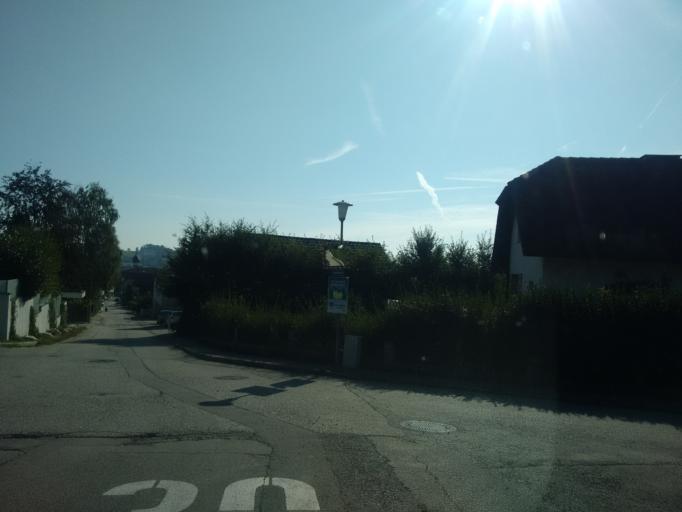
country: AT
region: Upper Austria
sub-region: Politischer Bezirk Linz-Land
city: Traun
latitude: 48.1367
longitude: 14.2239
